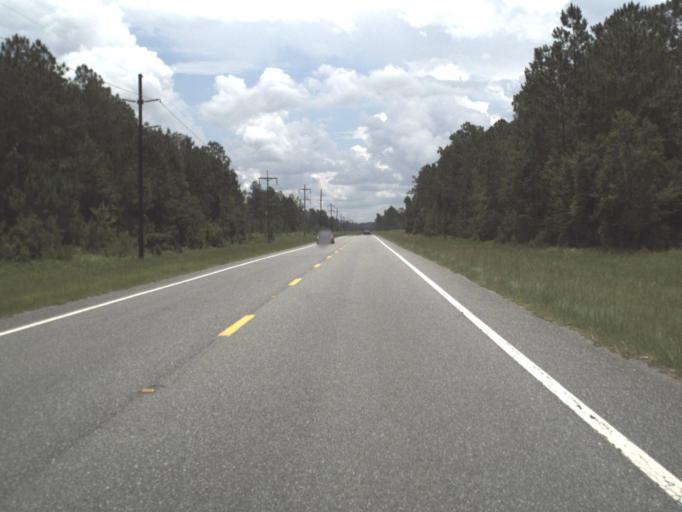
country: US
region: Florida
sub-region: Bradford County
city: Starke
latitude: 29.9763
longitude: -82.2251
